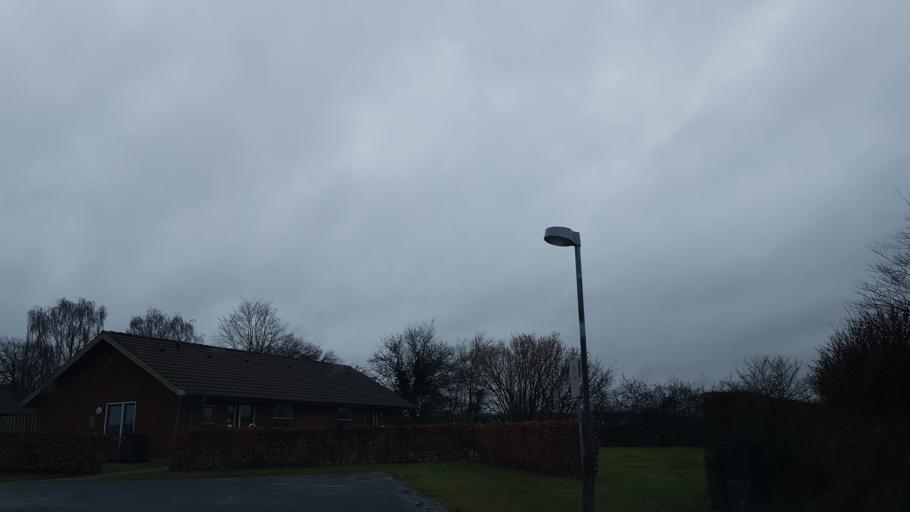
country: DK
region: South Denmark
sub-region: Kolding Kommune
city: Vamdrup
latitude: 55.3587
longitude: 9.1962
